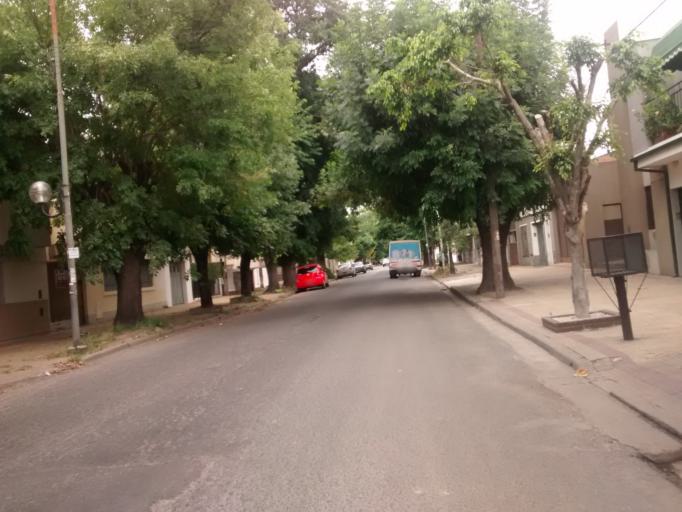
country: AR
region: Buenos Aires
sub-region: Partido de La Plata
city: La Plata
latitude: -34.9360
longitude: -57.9375
